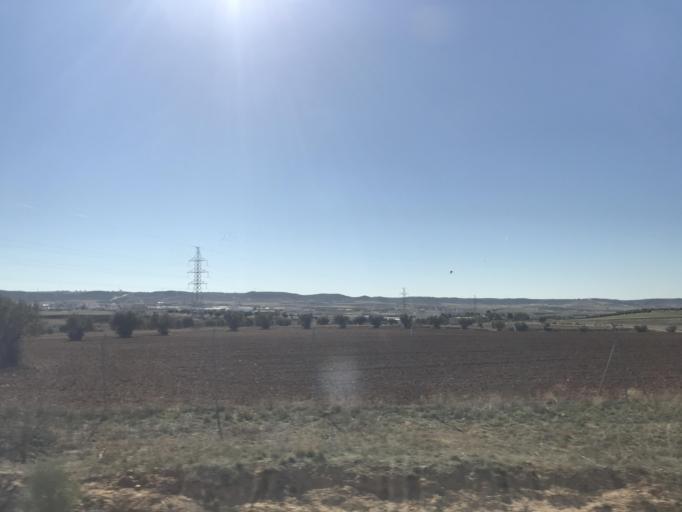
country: ES
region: Madrid
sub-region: Provincia de Madrid
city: Torres de la Alameda
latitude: 40.4265
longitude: -3.3828
